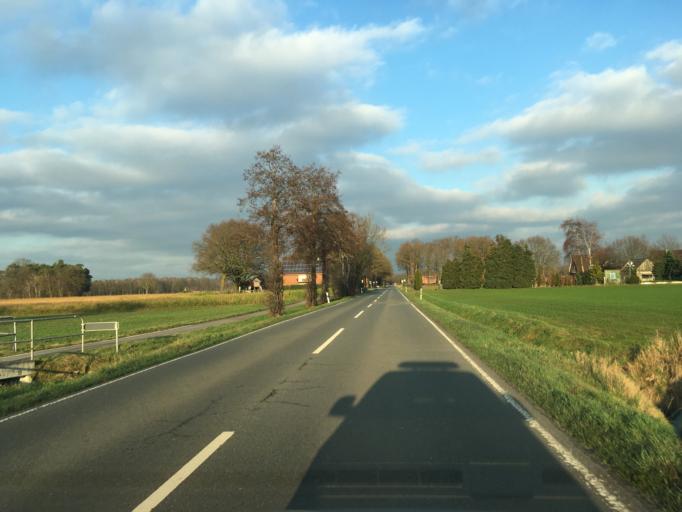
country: DE
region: North Rhine-Westphalia
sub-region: Regierungsbezirk Munster
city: Gronau
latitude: 52.1549
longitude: 7.0213
